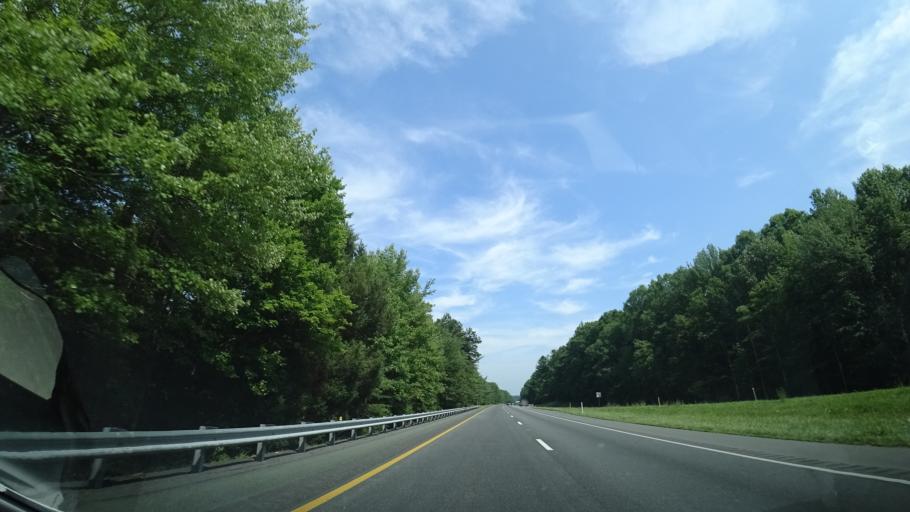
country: US
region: Virginia
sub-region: Louisa County
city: Louisa
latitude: 37.9388
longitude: -78.1057
